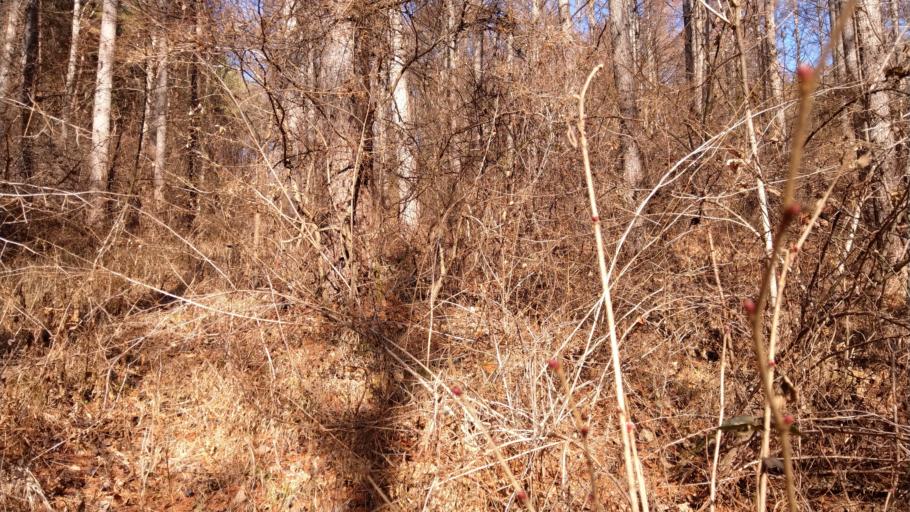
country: JP
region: Nagano
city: Komoro
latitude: 36.3771
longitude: 138.4366
